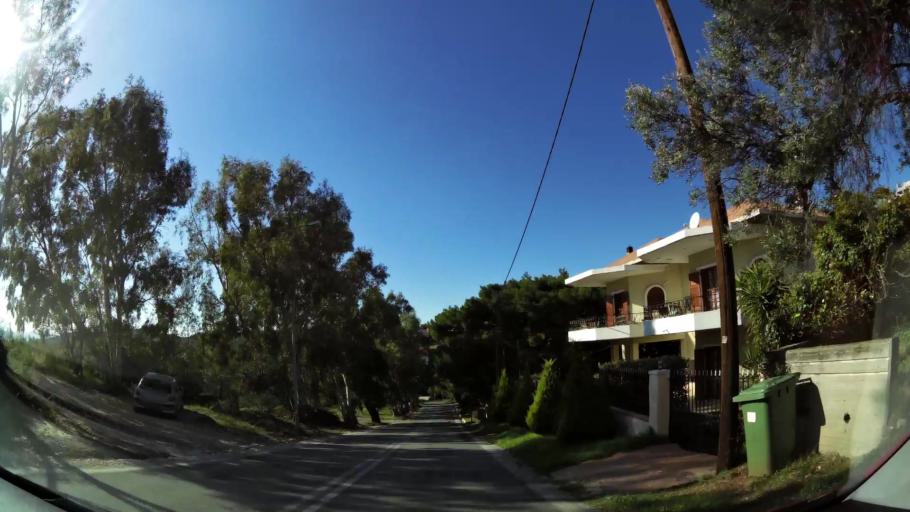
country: GR
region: Attica
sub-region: Nomarchia Athinas
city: Penteli
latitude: 38.0438
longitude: 23.8850
